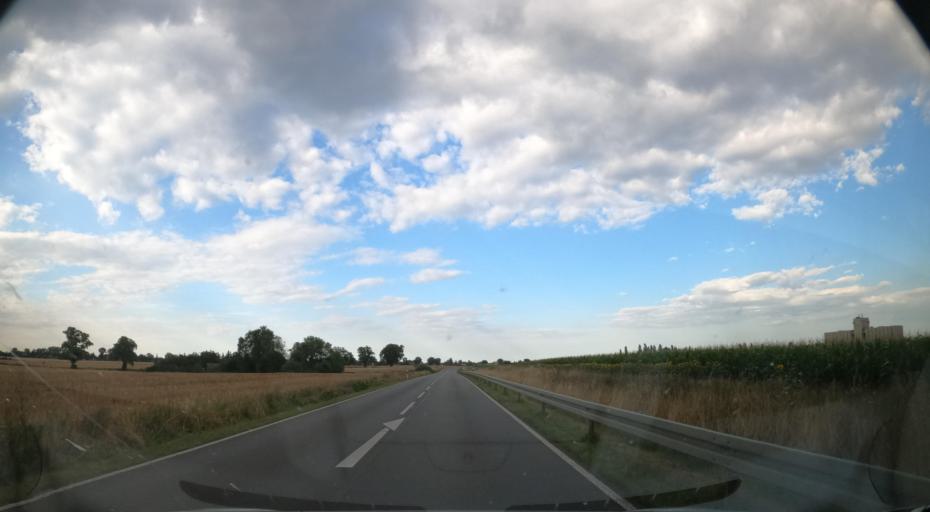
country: DE
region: Mecklenburg-Vorpommern
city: Pasewalk
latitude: 53.5126
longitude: 13.9710
